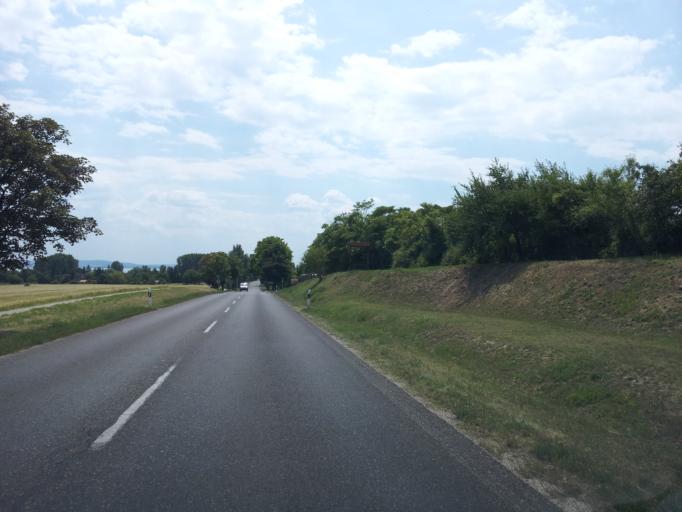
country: HU
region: Veszprem
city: Balatonfured
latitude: 46.9176
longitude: 17.8190
